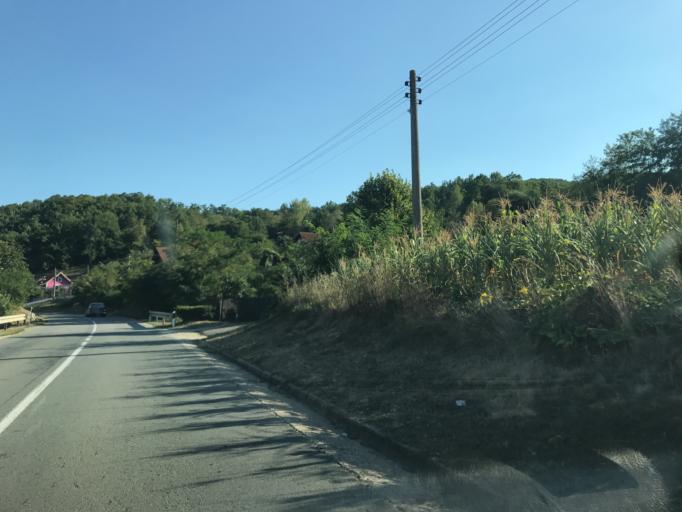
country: RO
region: Mehedinti
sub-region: Comuna Svinita
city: Svinita
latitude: 44.4512
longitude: 22.1697
